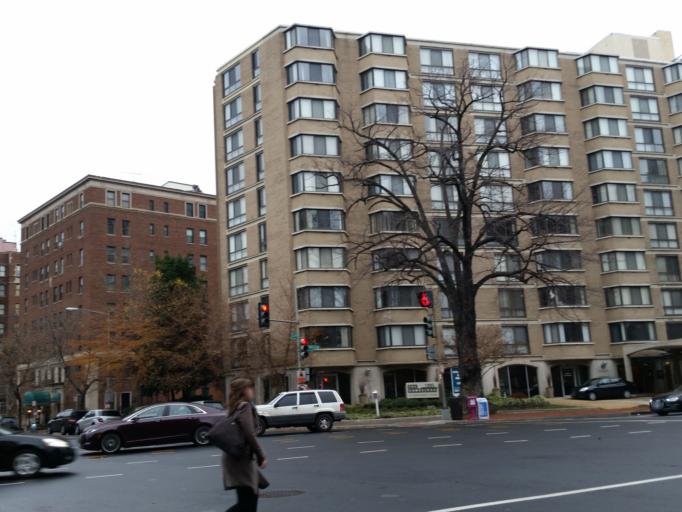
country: US
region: Washington, D.C.
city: Washington, D.C.
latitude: 38.9047
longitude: -77.0297
